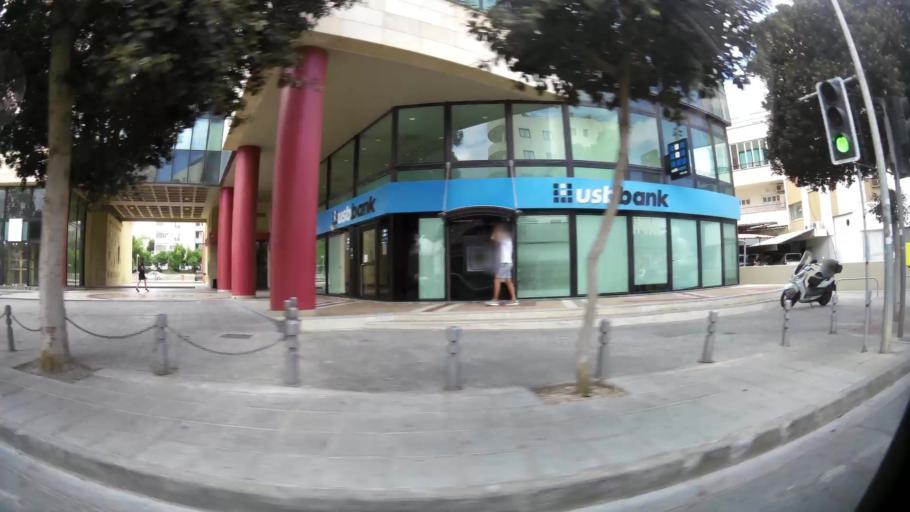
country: CY
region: Lefkosia
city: Nicosia
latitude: 35.1604
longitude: 33.3600
